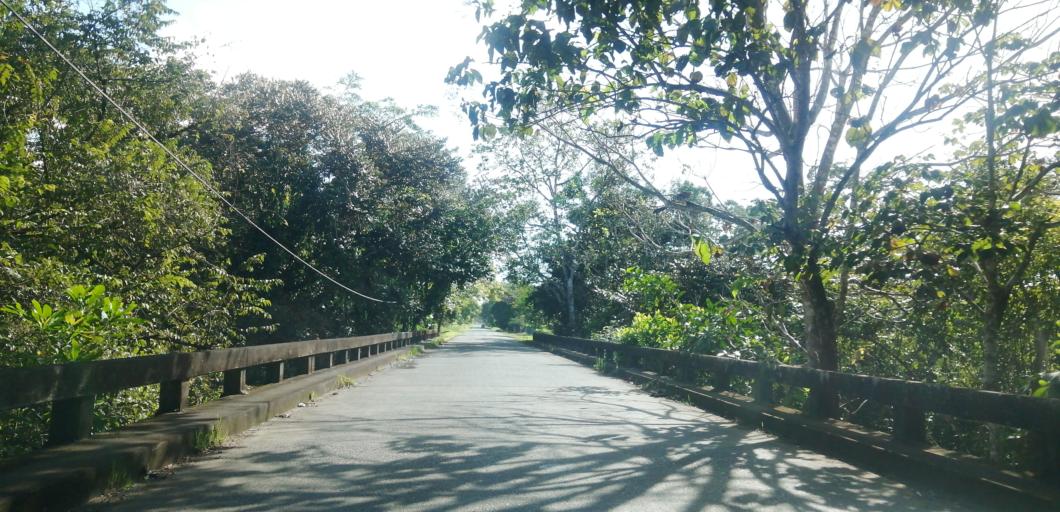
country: PA
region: Panama
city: Canita
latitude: 9.2190
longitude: -78.8484
